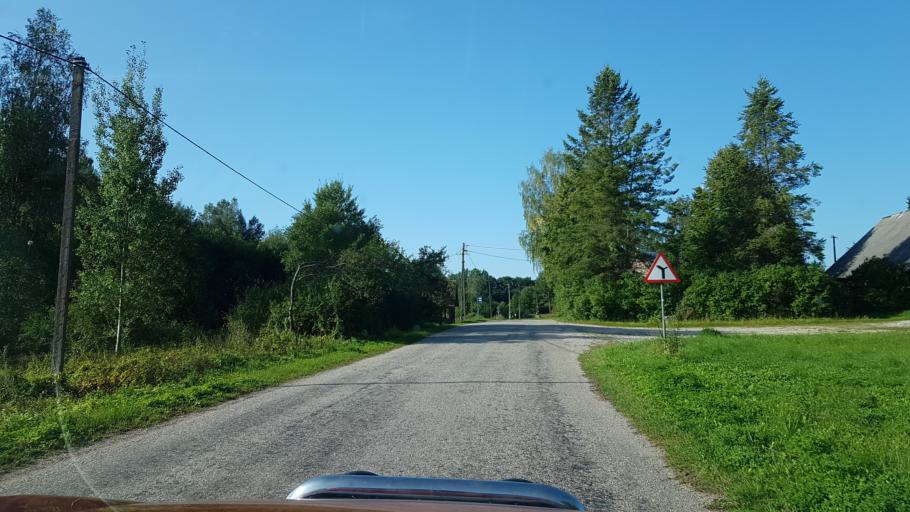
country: LV
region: Apes Novads
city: Ape
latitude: 57.6726
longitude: 26.6758
